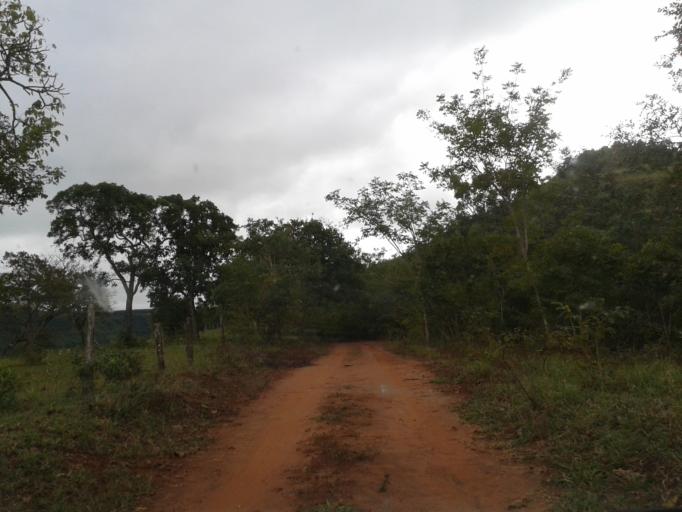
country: BR
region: Minas Gerais
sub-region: Campina Verde
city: Campina Verde
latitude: -19.4676
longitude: -49.6107
